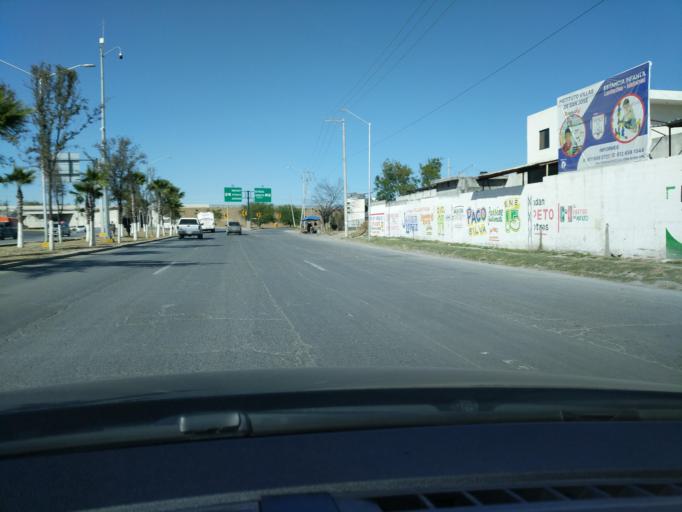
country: MX
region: Nuevo Leon
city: Juarez
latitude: 25.6575
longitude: -100.0790
